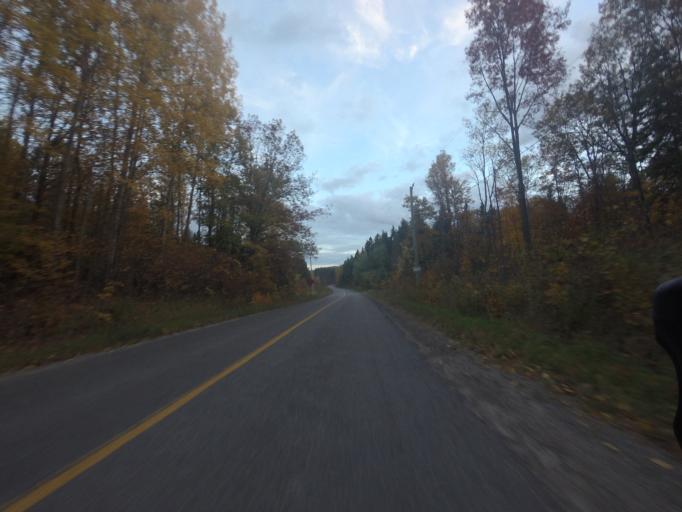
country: CA
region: Ontario
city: Renfrew
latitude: 45.3680
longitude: -76.9656
